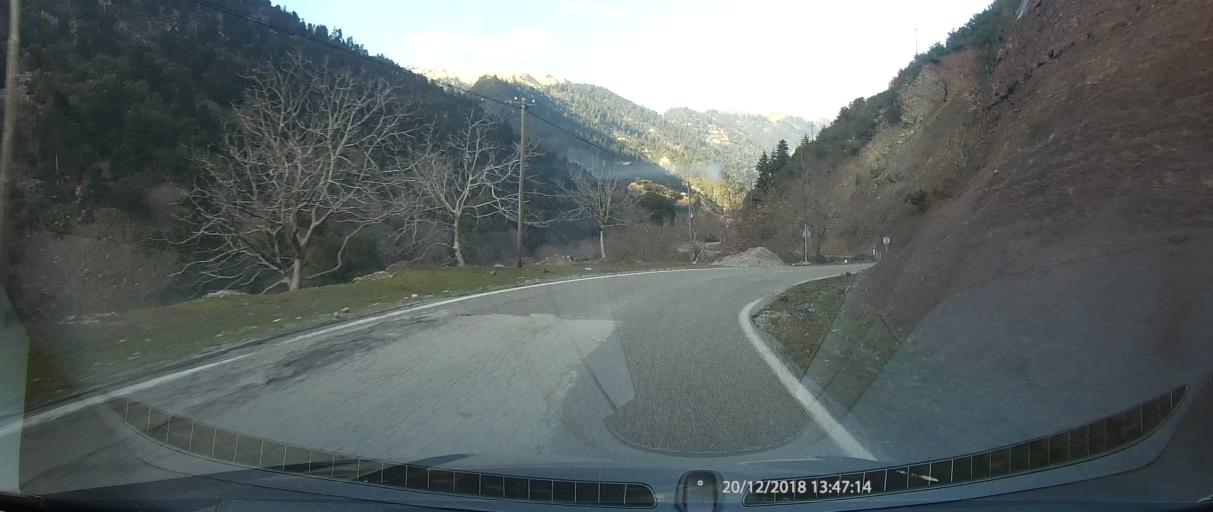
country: GR
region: West Greece
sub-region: Nomos Aitolias kai Akarnanias
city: Thermo
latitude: 38.6798
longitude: 21.6150
